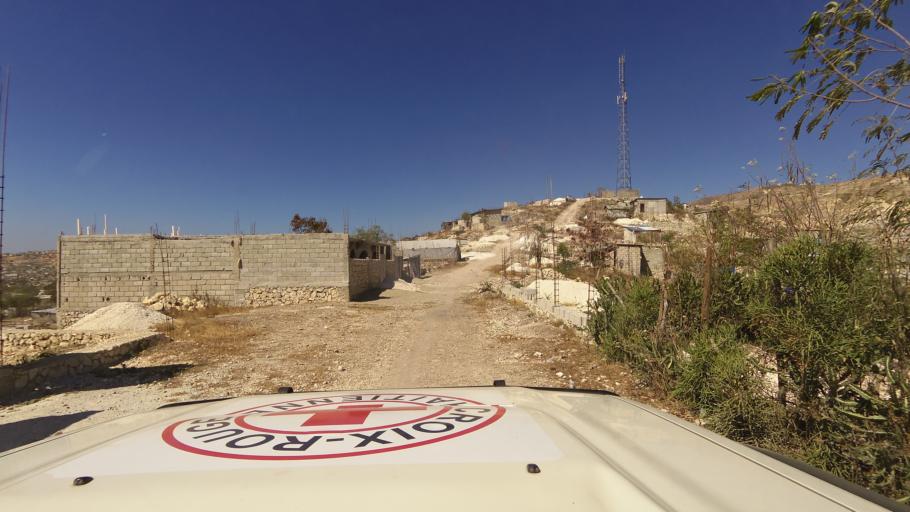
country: HT
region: Ouest
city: Croix des Bouquets
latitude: 18.6618
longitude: -72.2552
